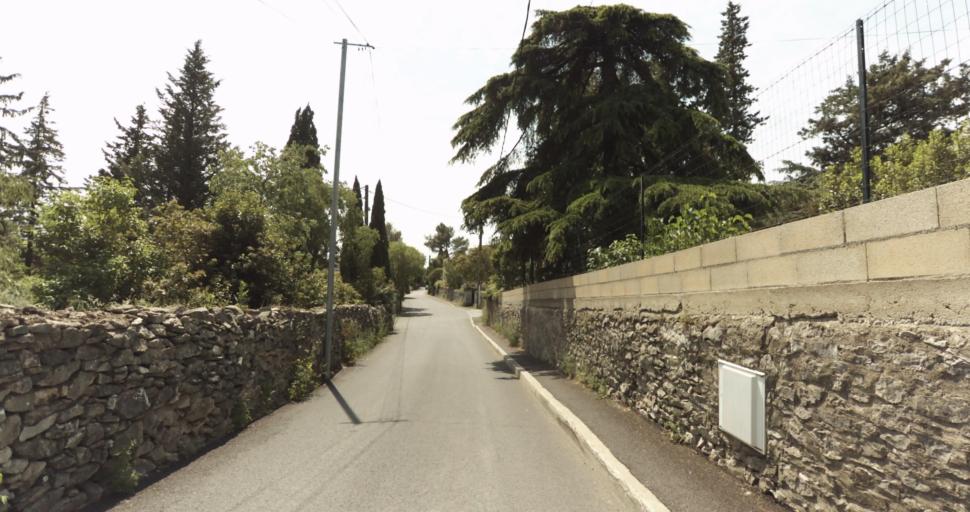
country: FR
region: Languedoc-Roussillon
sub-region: Departement du Gard
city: Nimes
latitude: 43.8526
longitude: 4.3484
